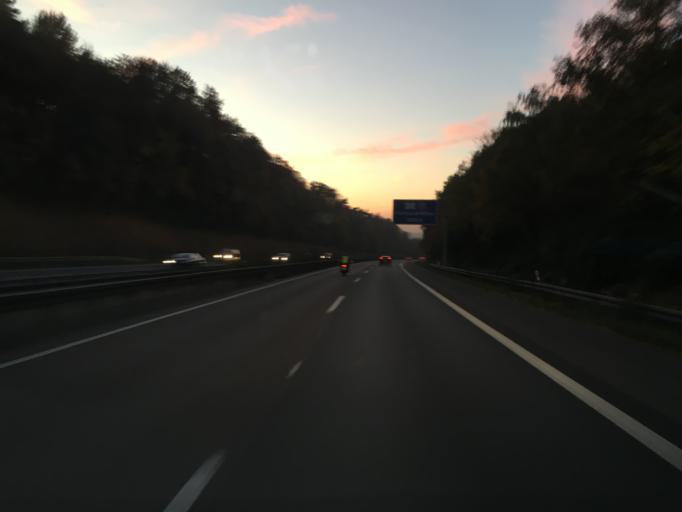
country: DE
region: North Rhine-Westphalia
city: Herdecke
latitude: 51.4445
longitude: 7.4356
